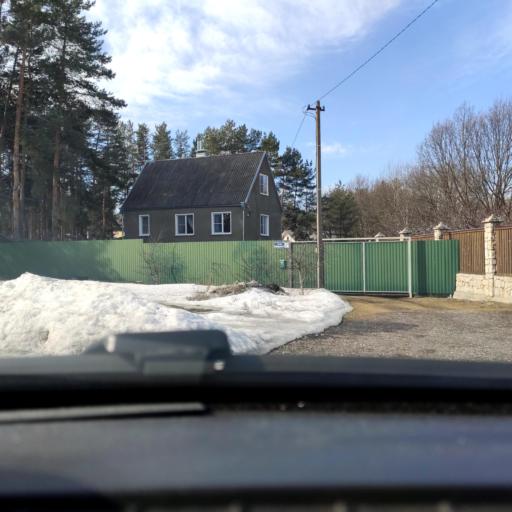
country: RU
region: Voronezj
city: Podgornoye
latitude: 51.7825
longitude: 39.1354
